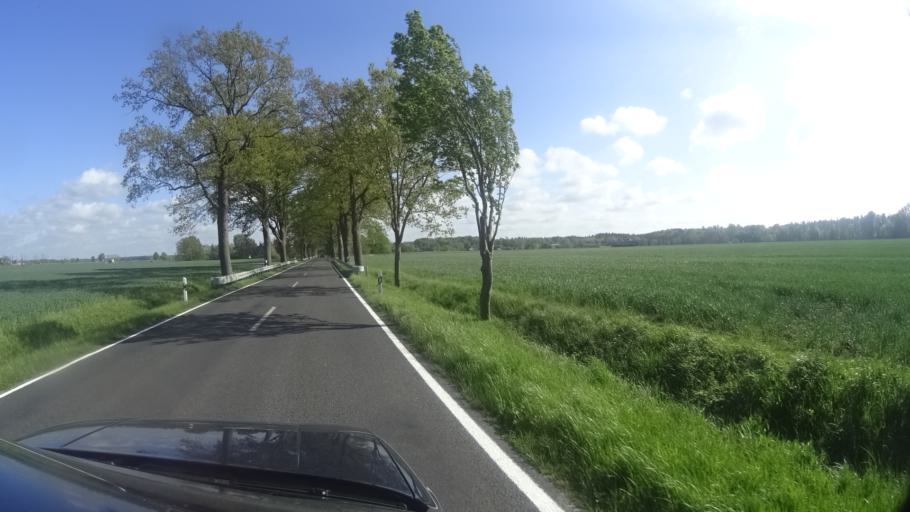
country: DE
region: Mecklenburg-Vorpommern
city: Gelbensande
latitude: 54.2432
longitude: 12.3181
